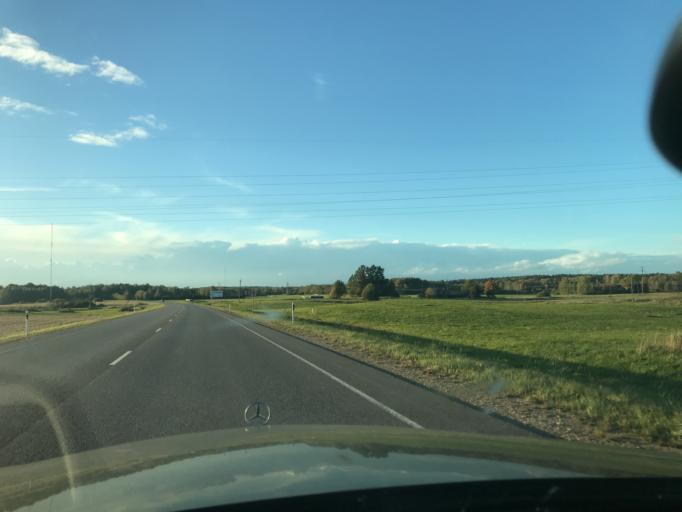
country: EE
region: Vorumaa
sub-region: Voru linn
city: Voru
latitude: 57.8551
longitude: 27.0235
